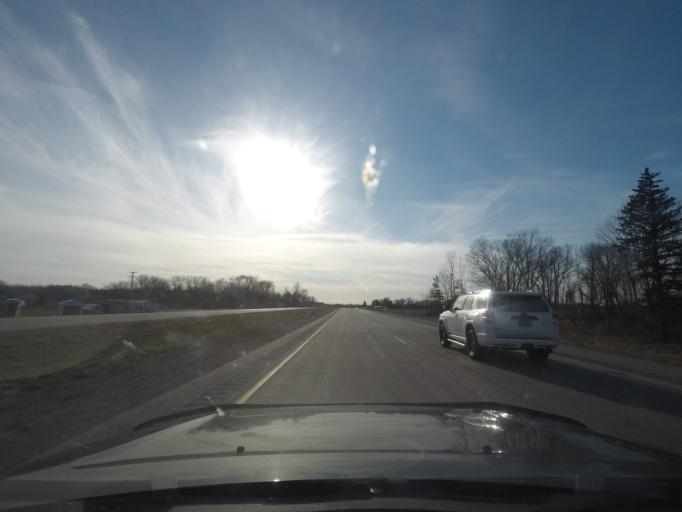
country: US
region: Indiana
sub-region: Marshall County
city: Plymouth
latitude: 41.4500
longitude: -86.2959
